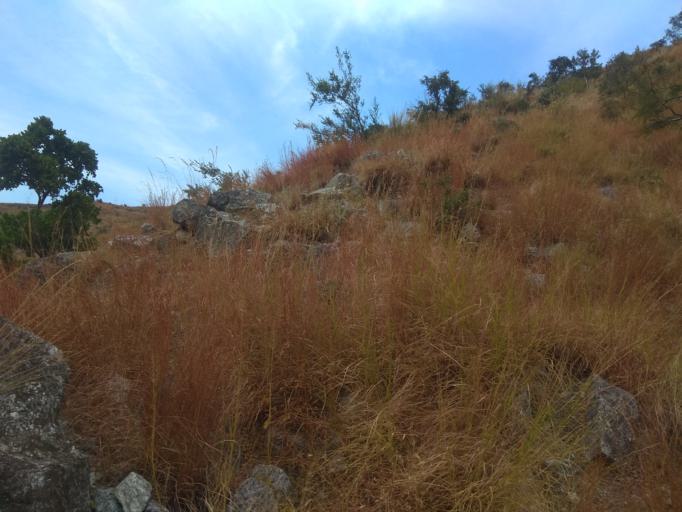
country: NP
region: Far Western
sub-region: Seti Zone
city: Achham
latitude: 29.2219
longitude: 81.6329
